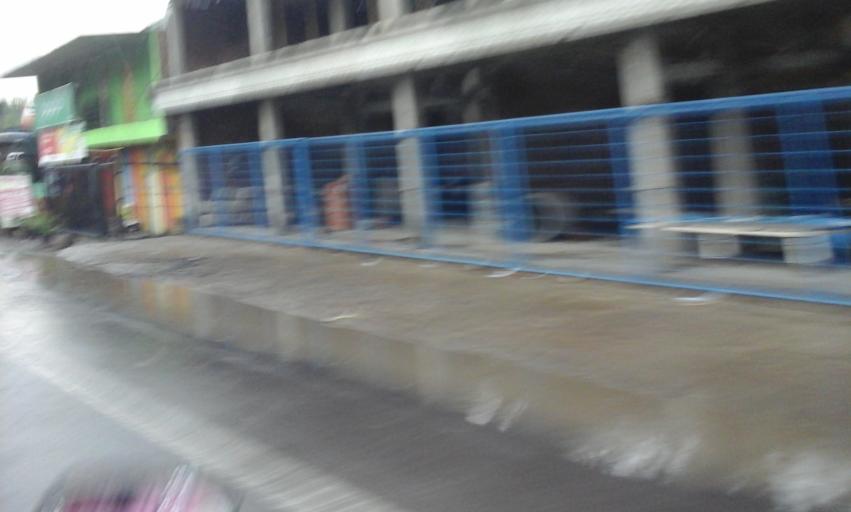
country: ID
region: East Java
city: Muktisari
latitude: -8.2140
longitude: 113.6806
